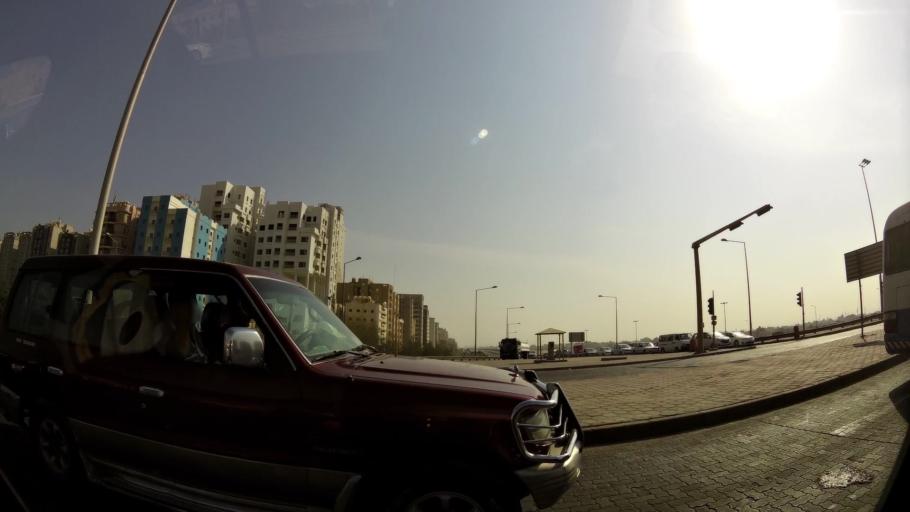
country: KW
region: Al Ahmadi
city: Al Fintas
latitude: 29.1610
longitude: 48.1112
